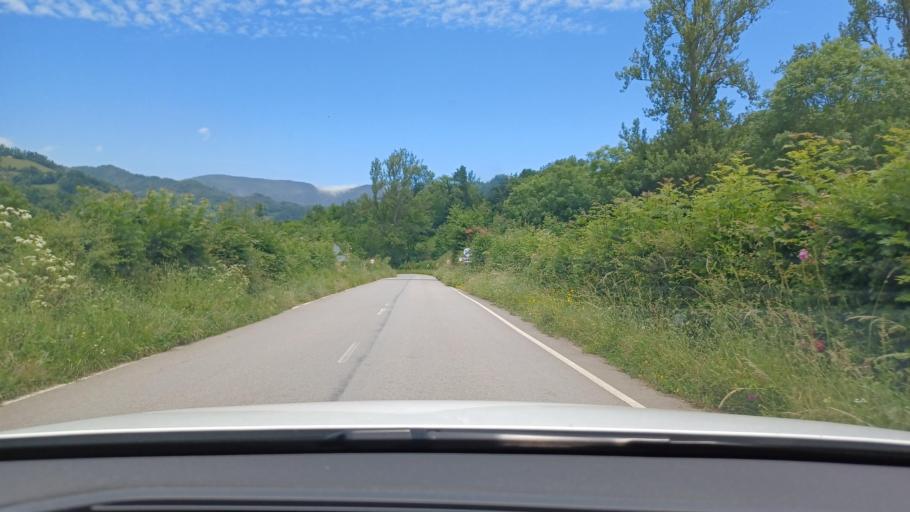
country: ES
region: Asturias
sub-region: Province of Asturias
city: La Plaza
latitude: 43.1468
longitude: -6.0864
